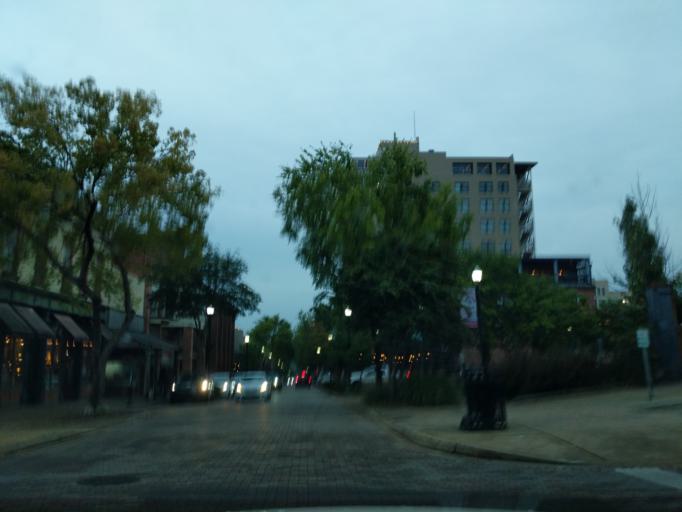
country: US
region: Mississippi
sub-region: Warren County
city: Vicksburg
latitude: 32.3490
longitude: -90.8823
